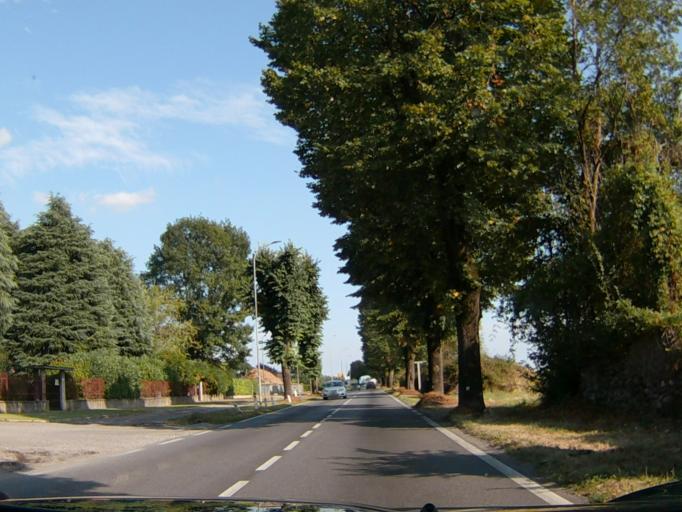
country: IT
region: Lombardy
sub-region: Provincia di Brescia
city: Palazzolo sull'Oglio
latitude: 45.5887
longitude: 9.9065
